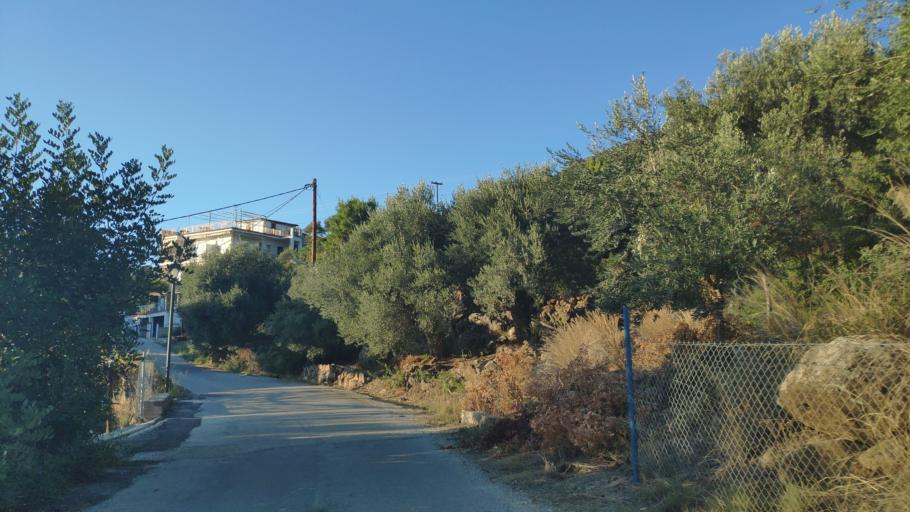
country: GR
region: Attica
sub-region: Nomos Piraios
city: Megalochori
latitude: 37.5941
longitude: 23.3403
